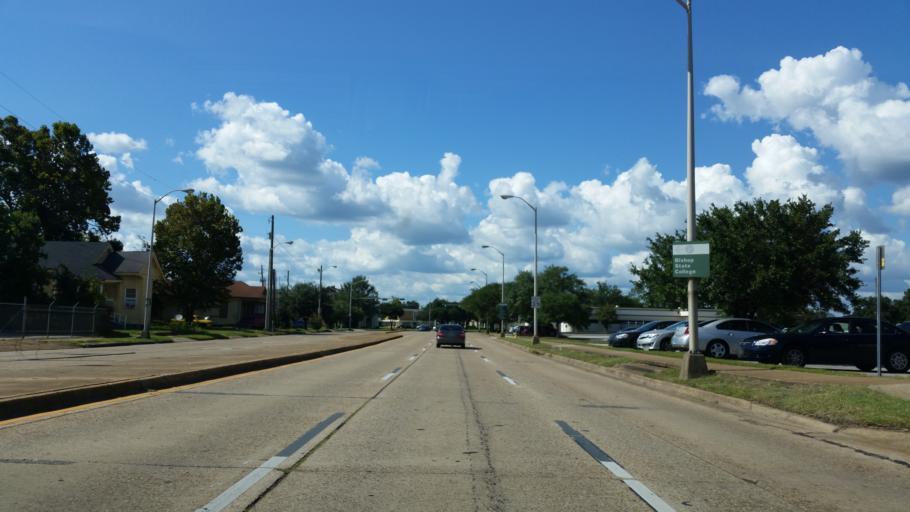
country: US
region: Alabama
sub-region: Mobile County
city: Mobile
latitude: 30.6912
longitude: -88.0560
